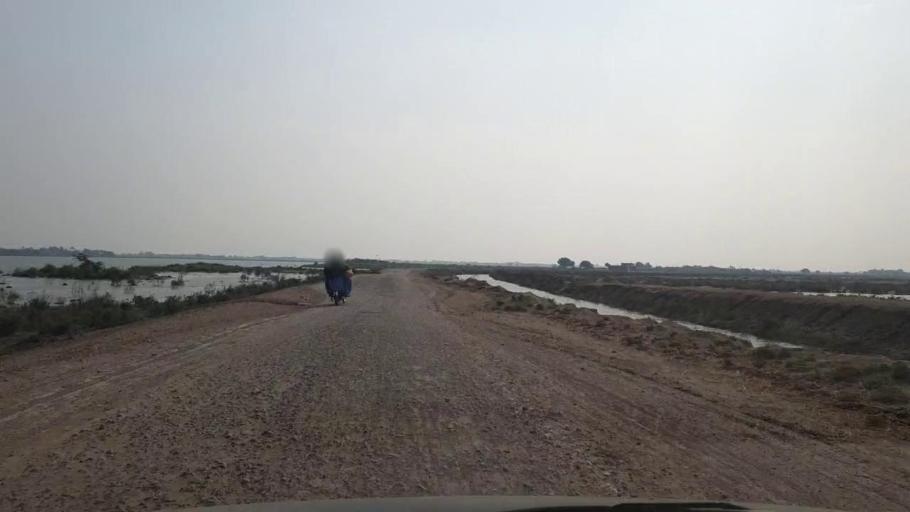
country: PK
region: Sindh
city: Tando Muhammad Khan
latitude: 25.0853
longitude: 68.3869
